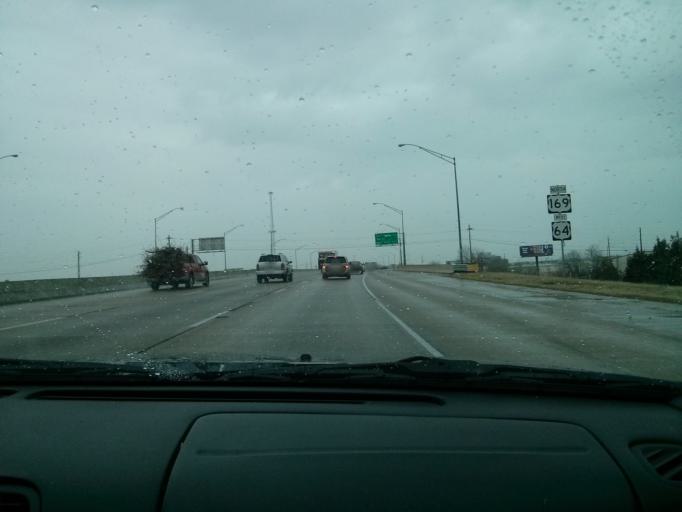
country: US
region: Oklahoma
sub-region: Tulsa County
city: Broken Arrow
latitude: 36.0819
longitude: -95.8593
